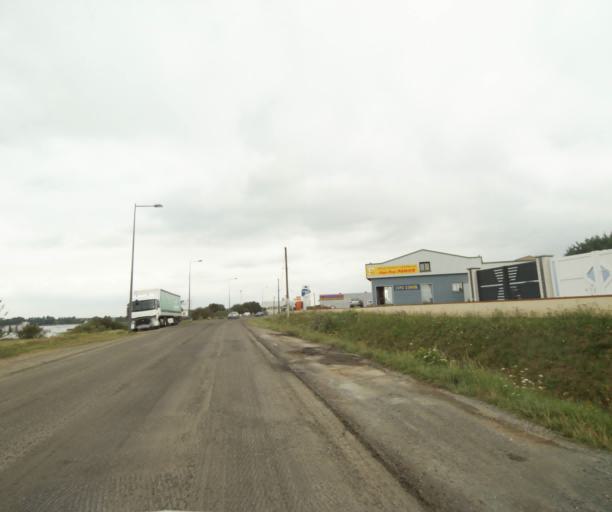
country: FR
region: Pays de la Loire
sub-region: Departement de la Sarthe
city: Solesmes
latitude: 47.8360
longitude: -0.2980
